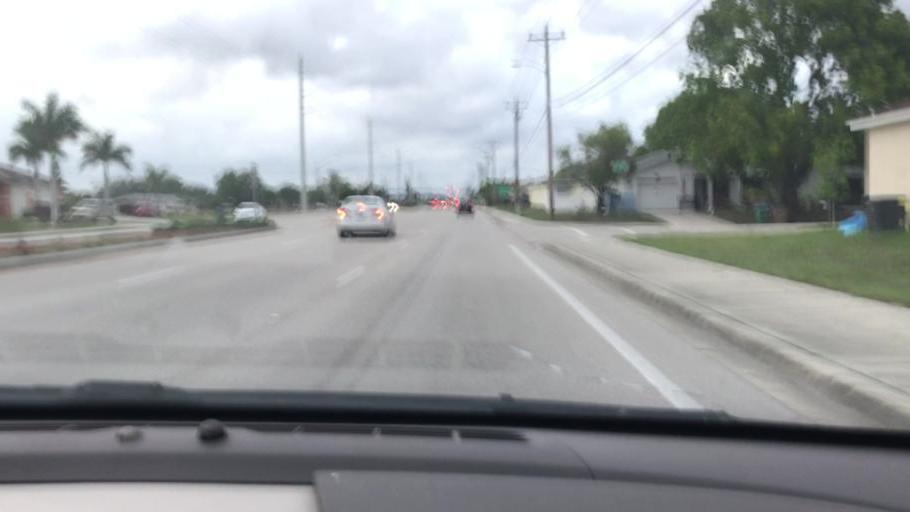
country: US
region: Florida
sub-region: Lee County
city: Lochmoor Waterway Estates
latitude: 26.6293
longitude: -81.9741
